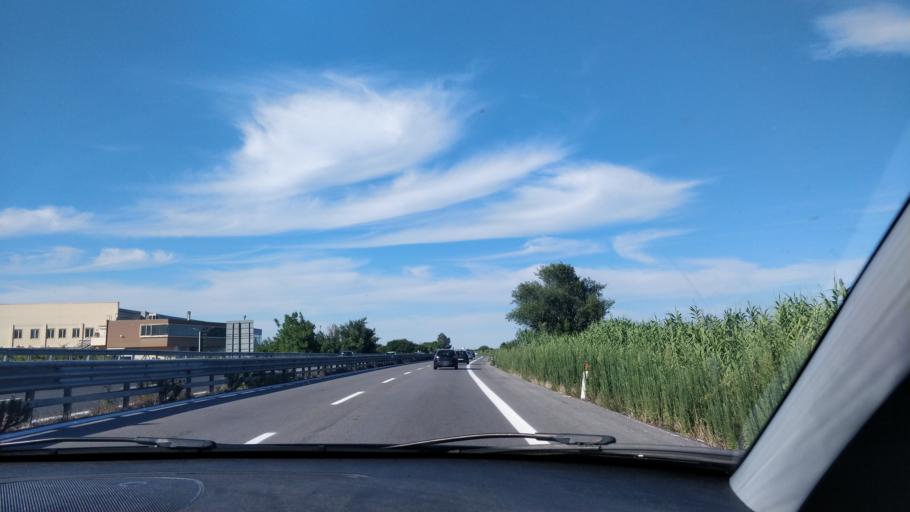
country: IT
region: Abruzzo
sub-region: Provincia di Pescara
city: Santa Teresa
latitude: 42.4233
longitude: 14.1720
